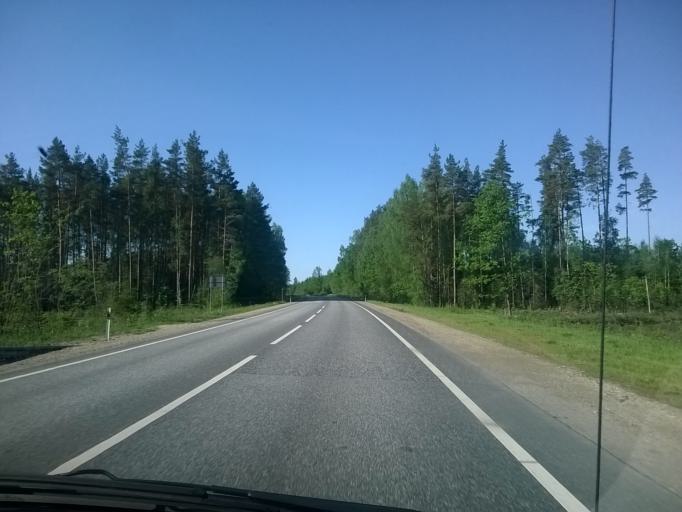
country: LV
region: Koceni
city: Koceni
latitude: 57.5397
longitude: 25.3741
